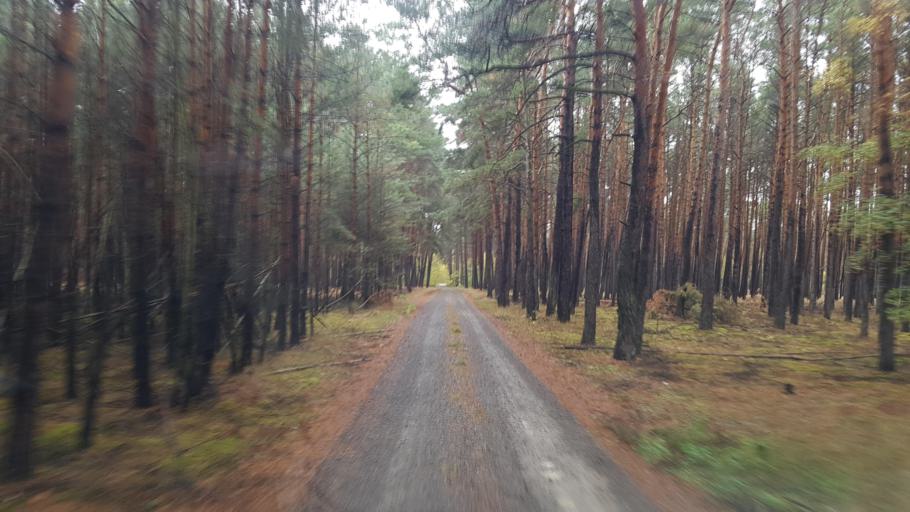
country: DE
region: Brandenburg
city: Schlieben
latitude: 51.7416
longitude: 13.3401
